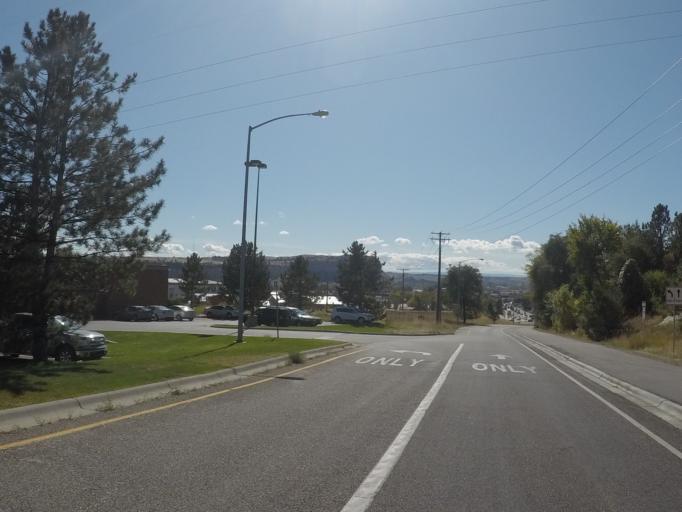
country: US
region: Montana
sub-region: Yellowstone County
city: Billings
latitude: 45.8021
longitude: -108.4810
